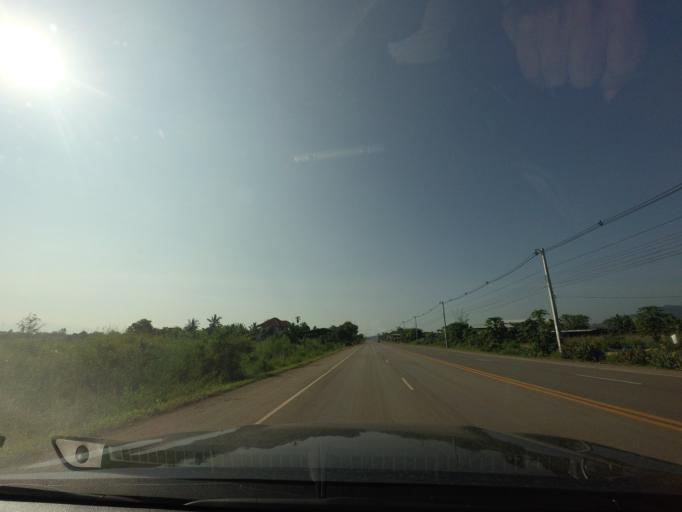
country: TH
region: Phetchabun
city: Lom Sak
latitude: 16.8206
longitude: 101.1815
